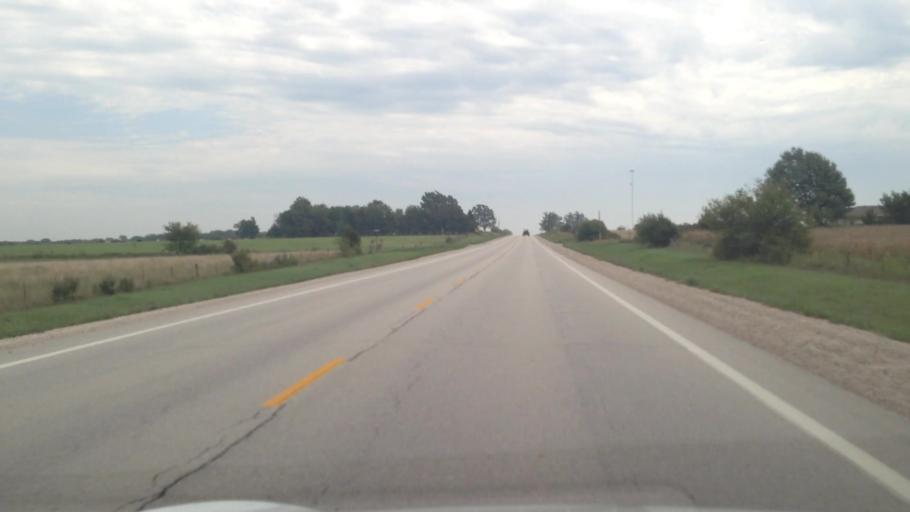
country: US
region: Kansas
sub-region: Anderson County
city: Garnett
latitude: 38.0816
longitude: -95.1896
